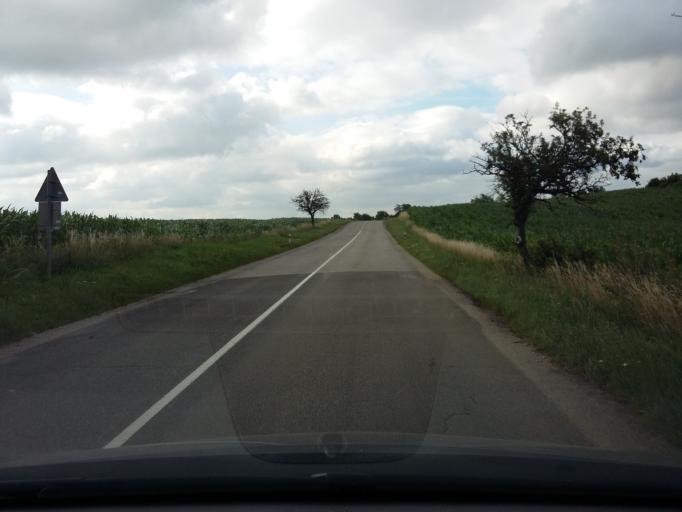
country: SK
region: Trnavsky
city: Smolenice
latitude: 48.5352
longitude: 17.4471
